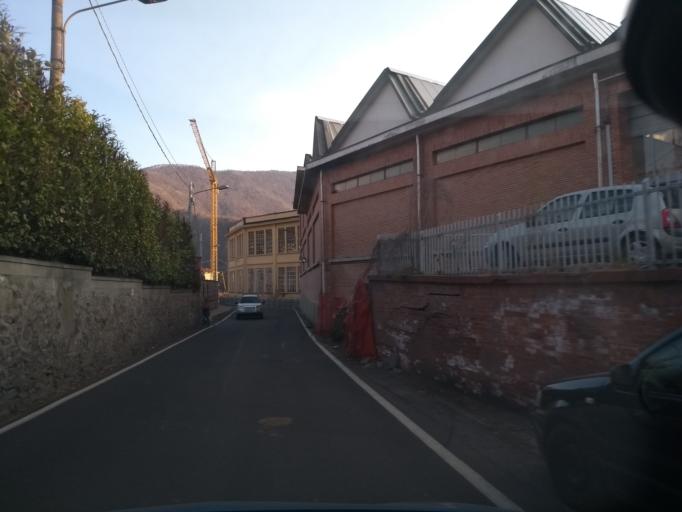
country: IT
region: Piedmont
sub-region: Provincia di Torino
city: Lanzo Torinese
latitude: 45.2755
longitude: 7.4814
